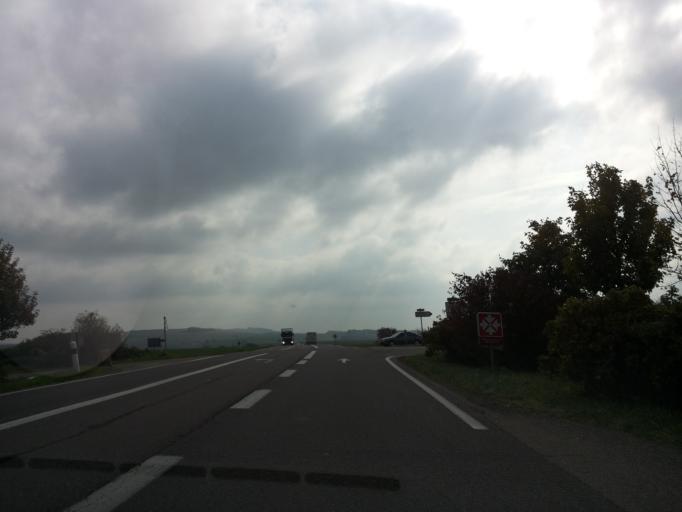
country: FR
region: Lorraine
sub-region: Departement de la Moselle
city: Solgne
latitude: 48.9572
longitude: 6.3003
